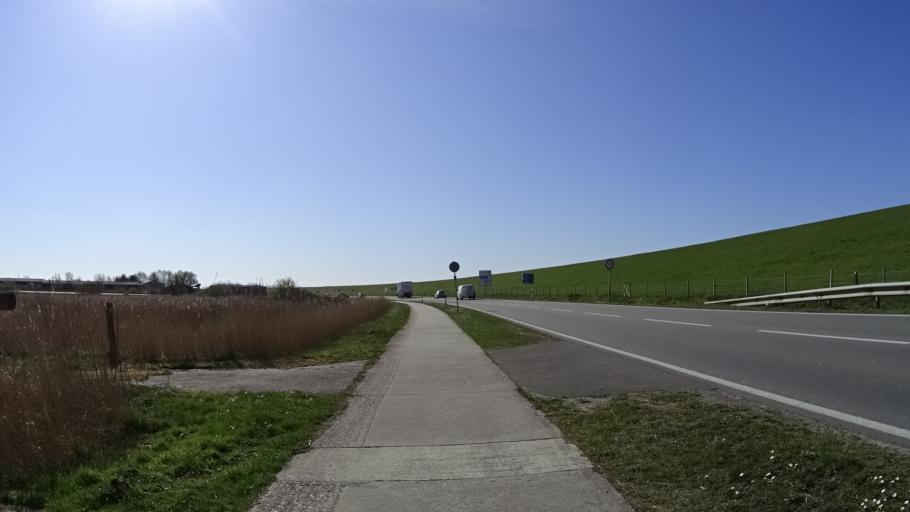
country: DE
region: Lower Saxony
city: Jemgum
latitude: 53.2384
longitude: 7.4075
